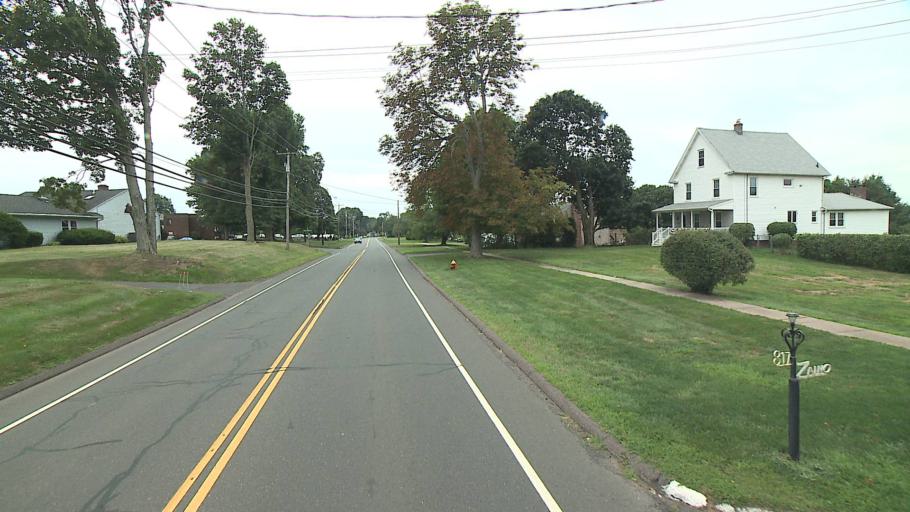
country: US
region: Connecticut
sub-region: Hartford County
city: Wethersfield
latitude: 41.6753
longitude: -72.6664
